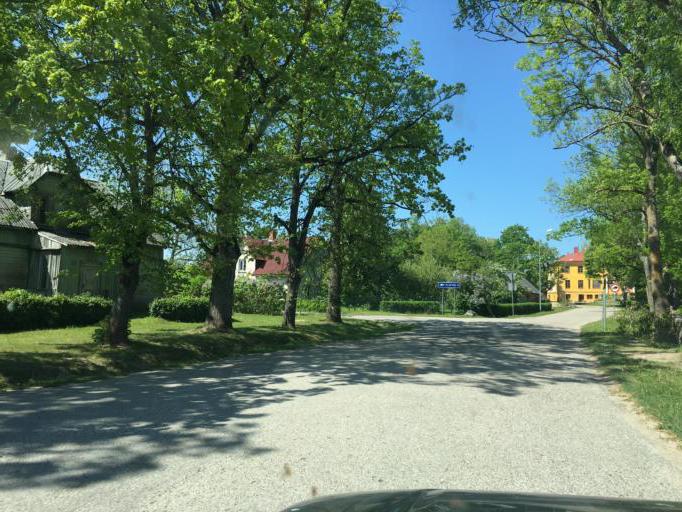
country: LV
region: Talsu Rajons
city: Valdemarpils
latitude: 57.4484
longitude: 22.5276
